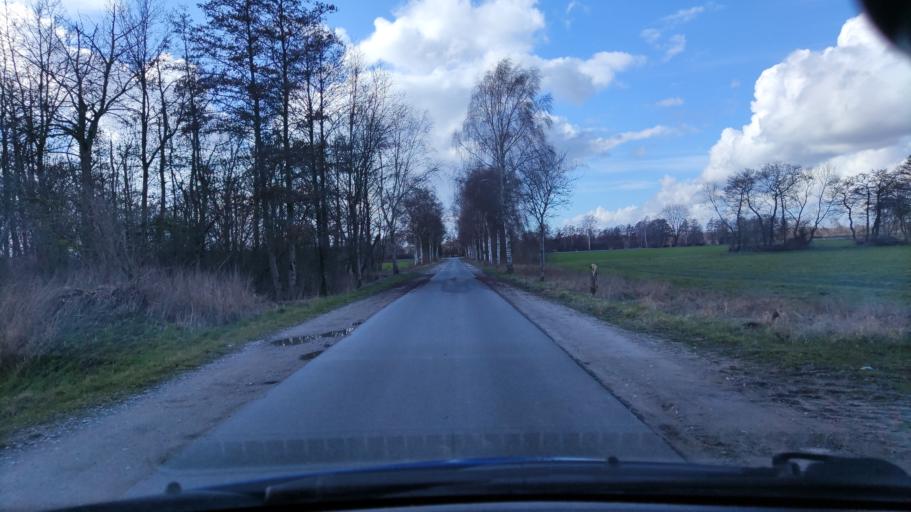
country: DE
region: Lower Saxony
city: Winsen
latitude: 53.3508
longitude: 10.1648
